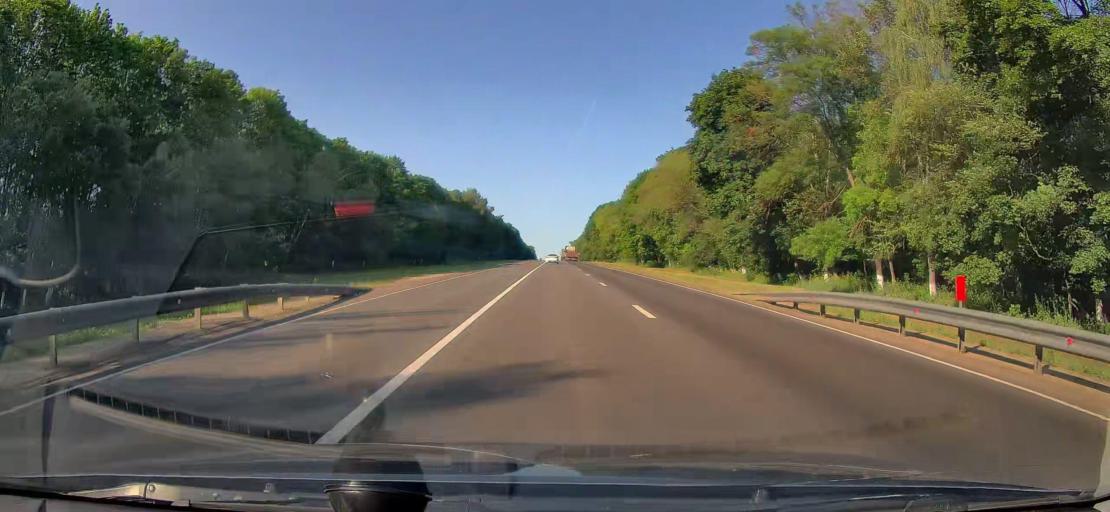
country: RU
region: Orjol
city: Mtsensk
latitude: 53.1967
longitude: 36.4331
